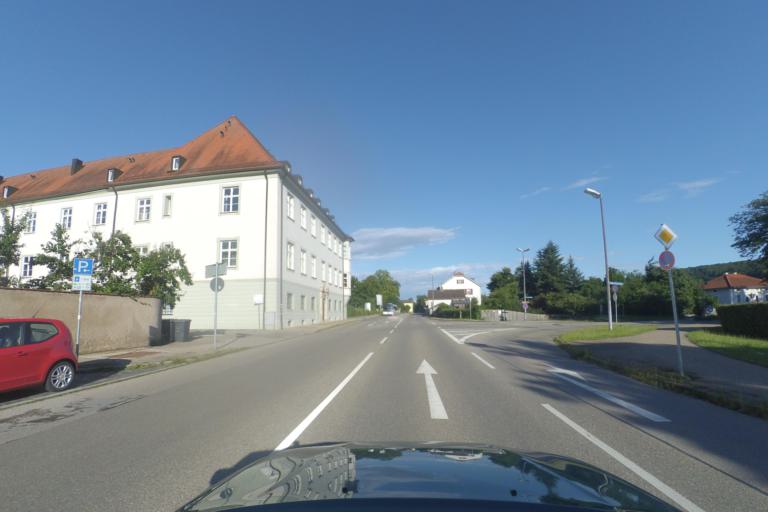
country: DE
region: Bavaria
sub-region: Upper Bavaria
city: Eichstaett
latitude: 48.8894
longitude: 11.1908
